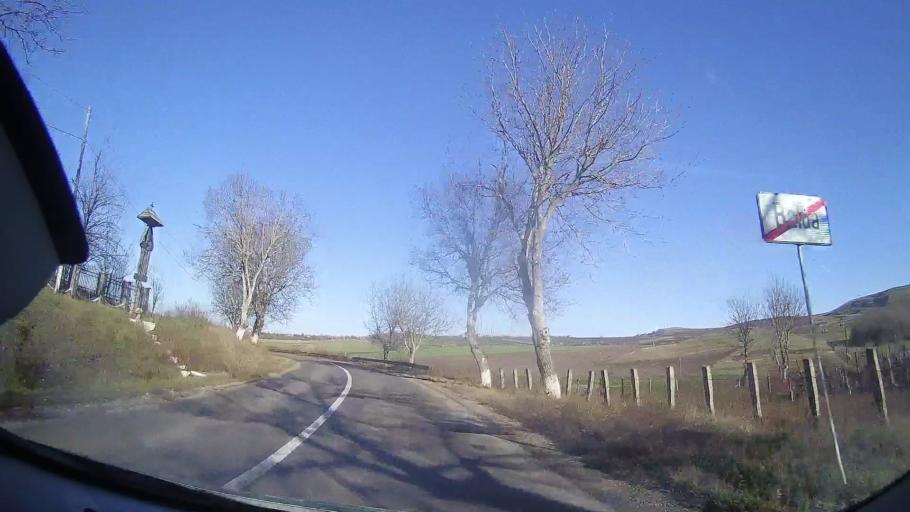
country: RO
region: Mures
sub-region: Comuna Sarmasu
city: Balda
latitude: 46.7357
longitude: 24.1491
